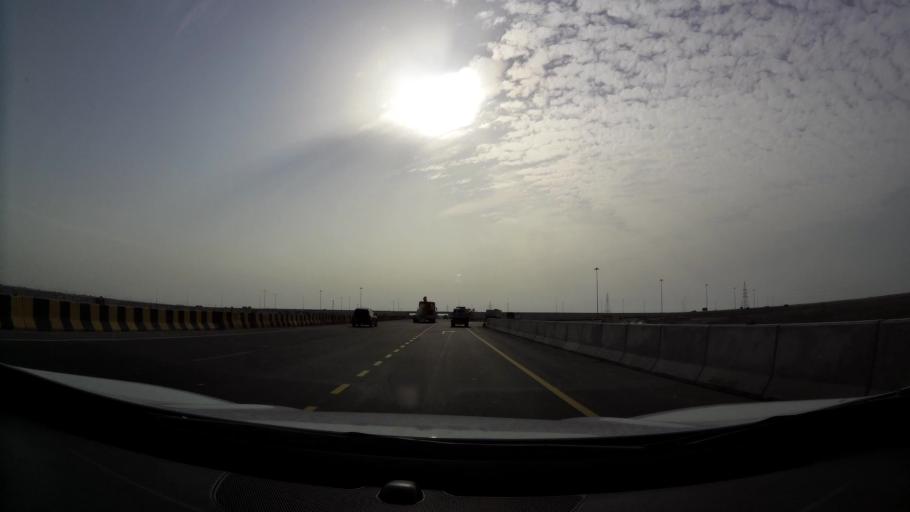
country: AE
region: Abu Dhabi
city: Abu Dhabi
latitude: 24.2160
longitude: 54.4203
